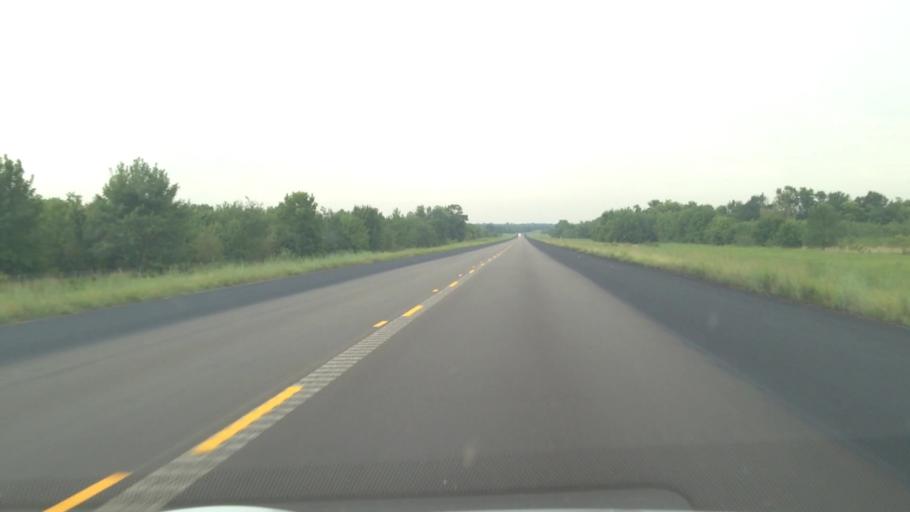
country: US
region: Kansas
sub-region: Cherokee County
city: Baxter Springs
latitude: 37.0418
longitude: -94.7105
